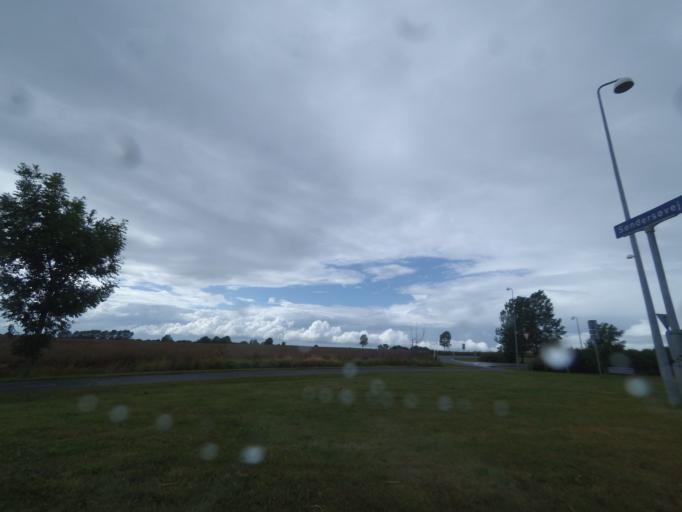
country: DK
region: South Denmark
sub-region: Nordfyns Kommune
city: Sonderso
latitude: 55.4840
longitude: 10.2421
